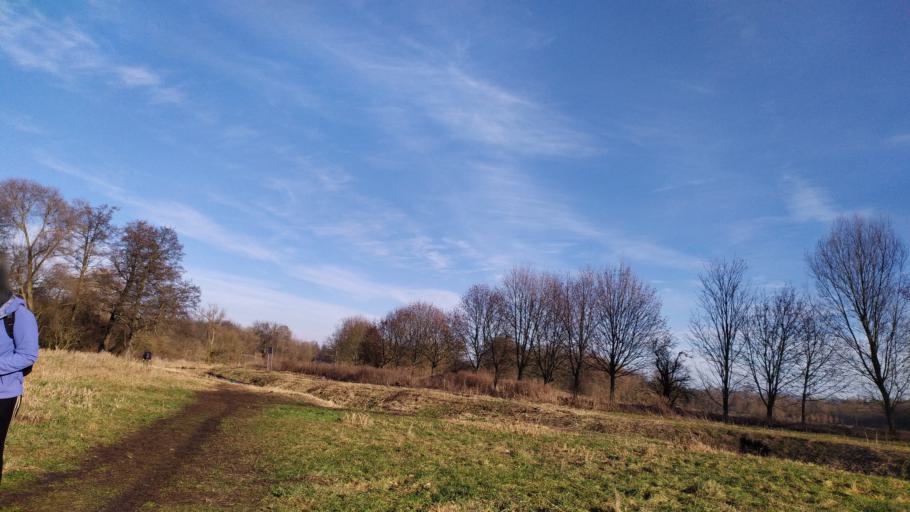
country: DE
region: Berlin
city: Friedrichshagen
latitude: 52.4773
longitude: 13.6341
